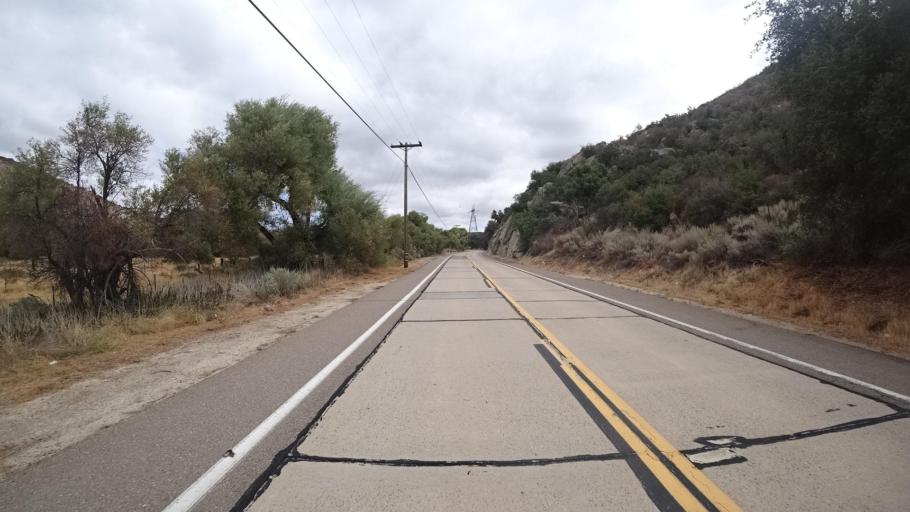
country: US
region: California
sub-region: San Diego County
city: Campo
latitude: 32.7234
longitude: -116.4368
